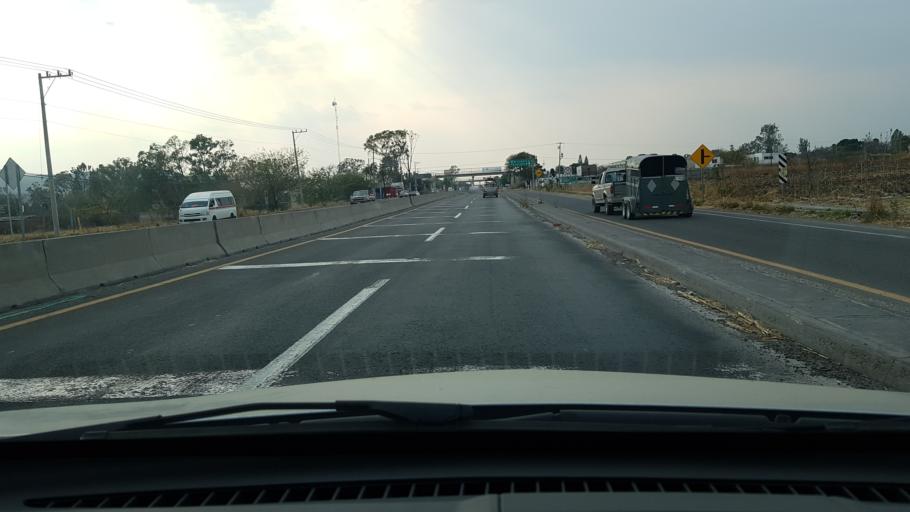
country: MX
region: Morelos
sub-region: Ayala
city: Unidad Habitacional Mariano Matamoros
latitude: 18.7442
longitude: -98.8382
